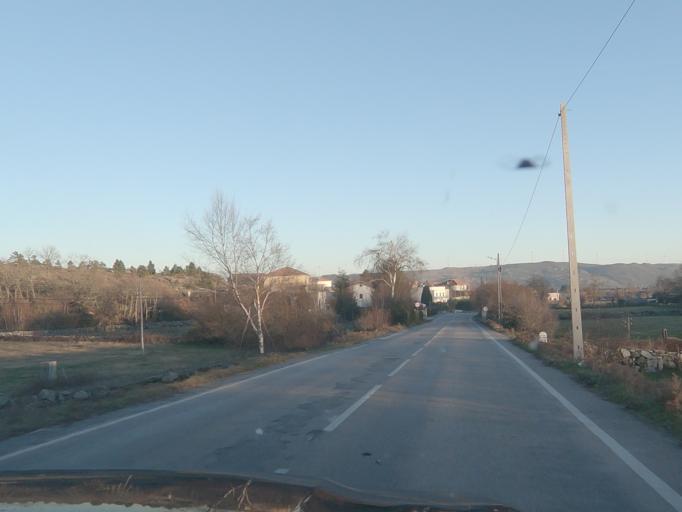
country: PT
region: Vila Real
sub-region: Vila Pouca de Aguiar
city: Vila Pouca de Aguiar
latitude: 41.5004
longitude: -7.6860
